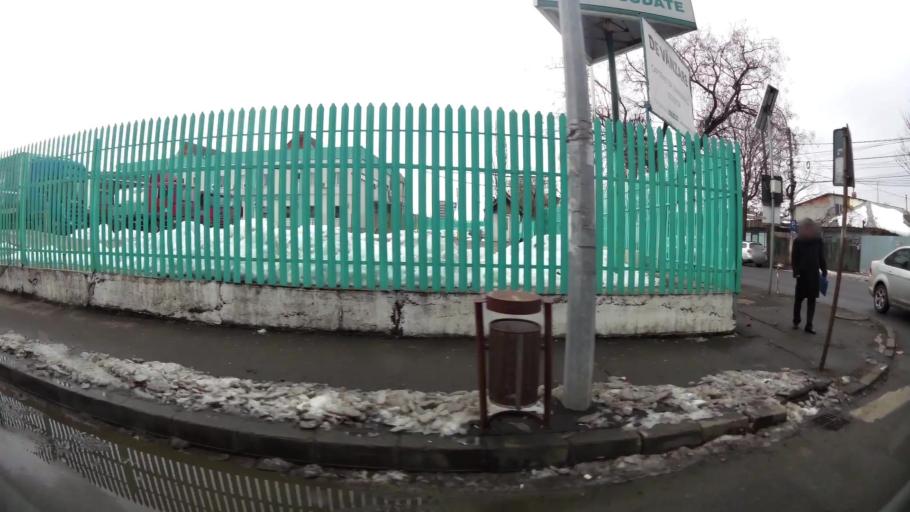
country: RO
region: Ilfov
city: Dobroesti
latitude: 44.4369
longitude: 26.1895
